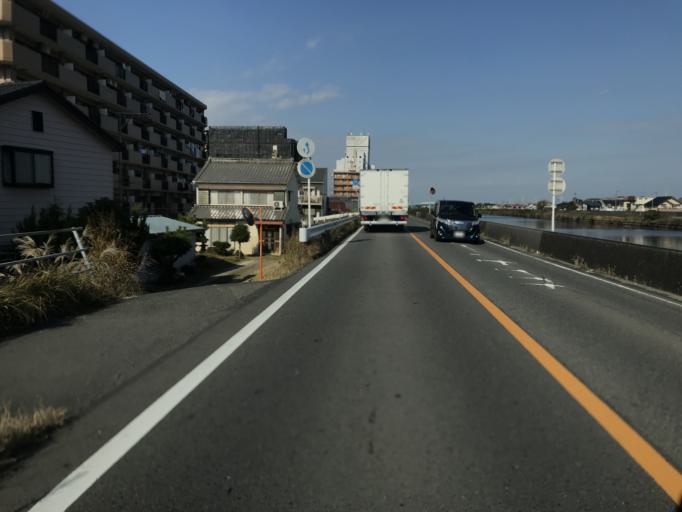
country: JP
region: Aichi
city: Kanie
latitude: 35.1608
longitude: 136.8255
